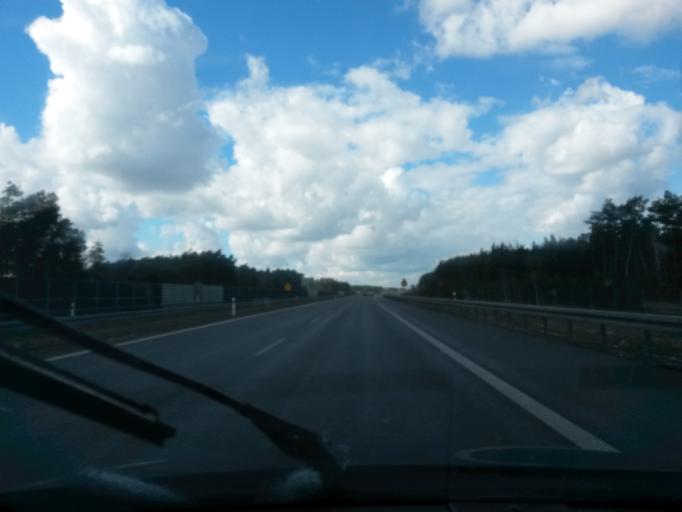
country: PL
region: Greater Poland Voivodeship
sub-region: Powiat kolski
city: Dabie
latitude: 52.0753
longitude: 18.8065
